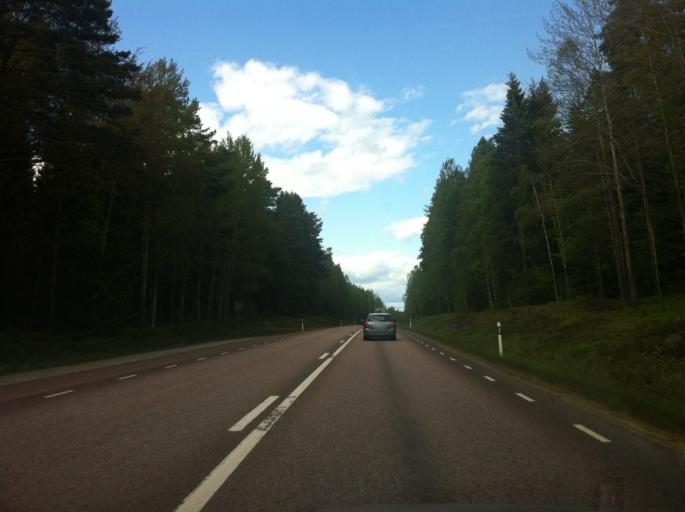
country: SE
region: Vaermland
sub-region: Kristinehamns Kommun
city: Kristinehamn
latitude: 59.3251
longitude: 14.1186
